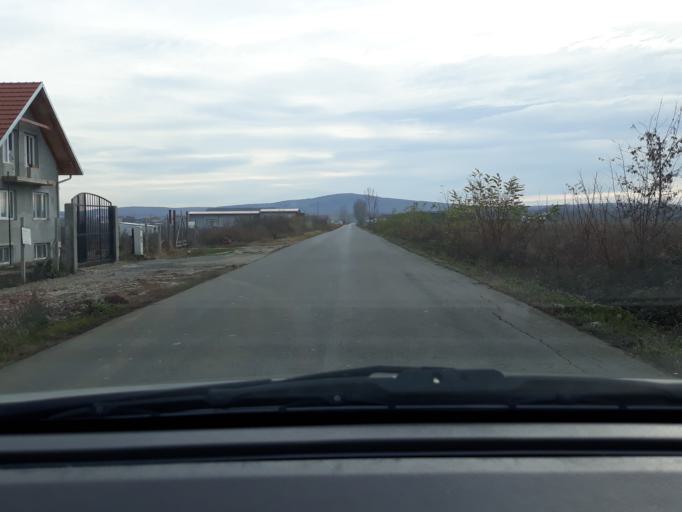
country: RO
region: Bihor
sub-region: Comuna Sanmartin
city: Sanmartin
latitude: 47.0274
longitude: 22.0026
